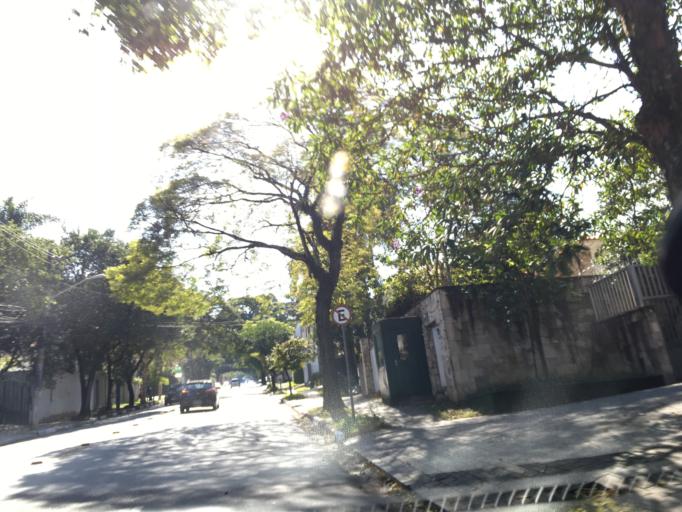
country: BR
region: Sao Paulo
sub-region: Sao Paulo
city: Sao Paulo
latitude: -23.5406
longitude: -46.7120
